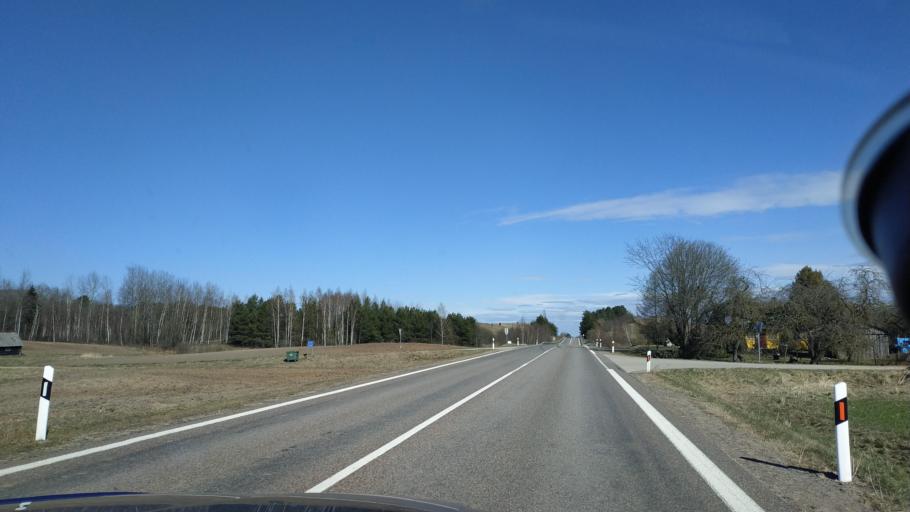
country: LT
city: Aukstadvaris
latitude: 54.5758
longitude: 24.4304
